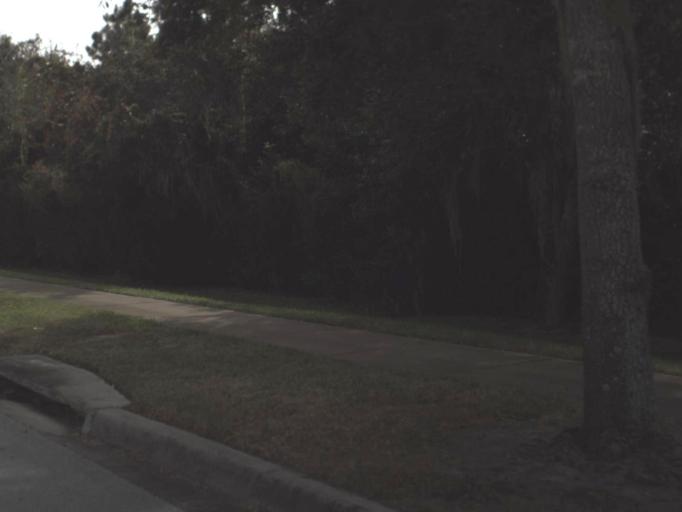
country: US
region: Florida
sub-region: Orange County
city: Taft
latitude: 28.4164
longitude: -81.2432
